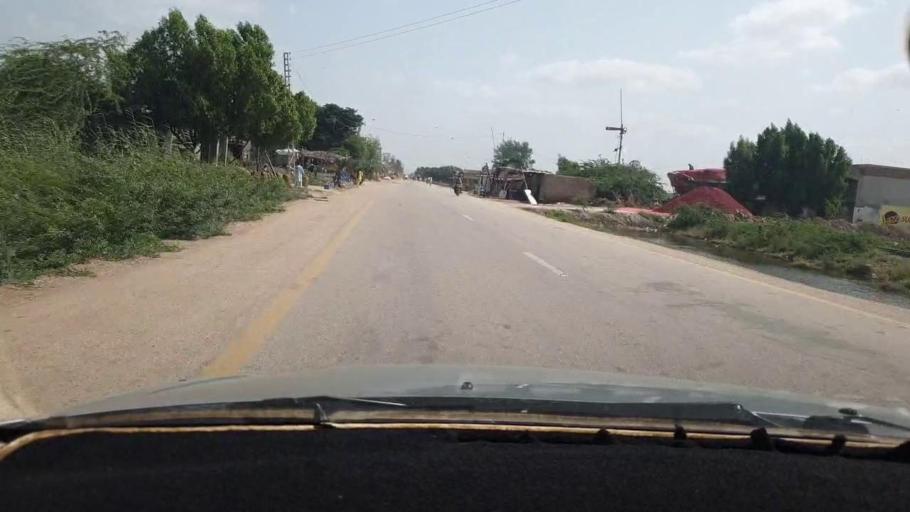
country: PK
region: Sindh
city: Naukot
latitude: 24.9762
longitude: 69.2951
